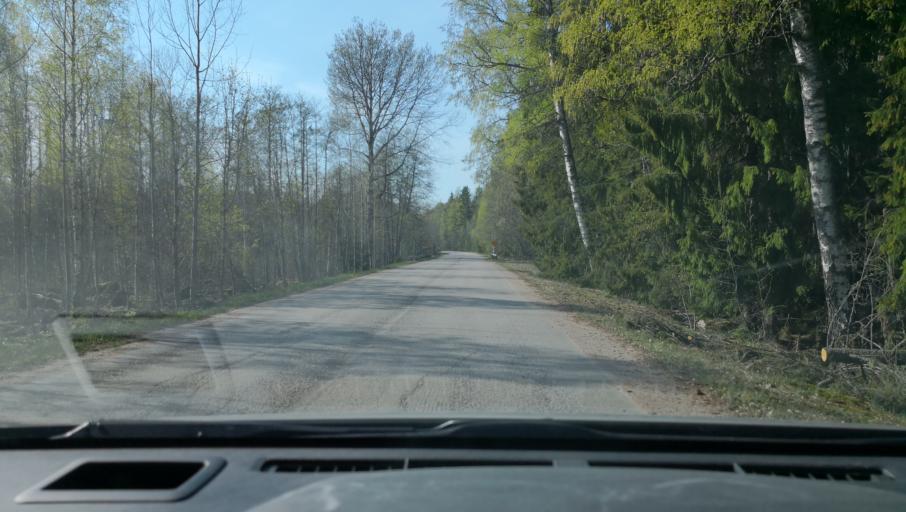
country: SE
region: Uppsala
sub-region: Heby Kommun
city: Tarnsjo
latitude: 60.2641
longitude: 16.9269
